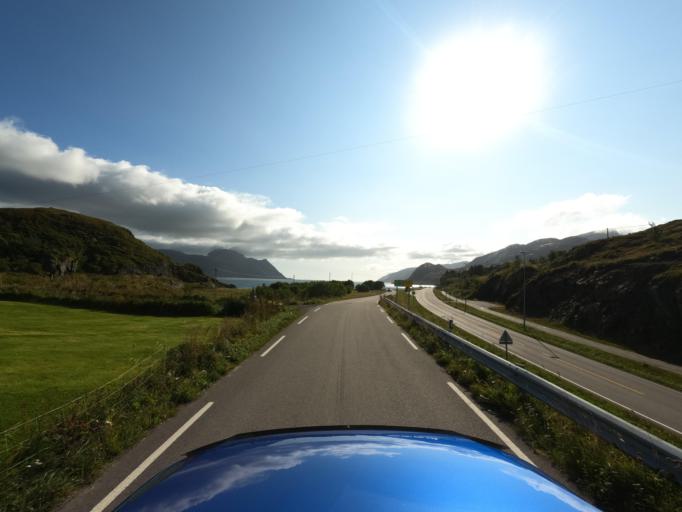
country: NO
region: Nordland
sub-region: Vestvagoy
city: Gravdal
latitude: 68.1399
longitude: 13.4561
